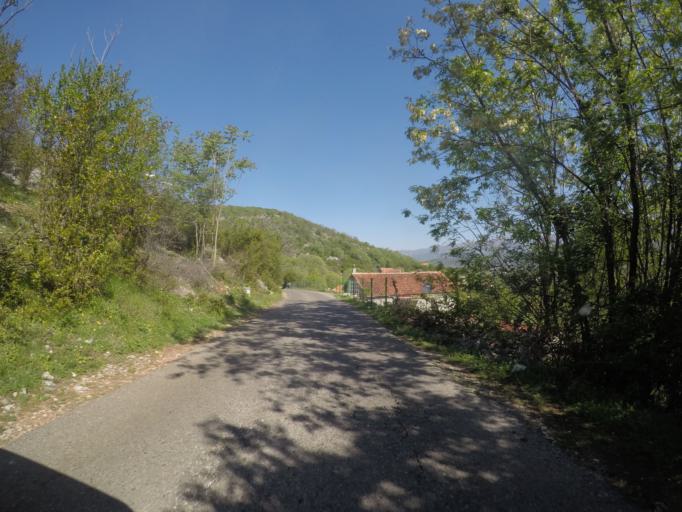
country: ME
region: Danilovgrad
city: Danilovgrad
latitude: 42.5329
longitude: 19.0899
